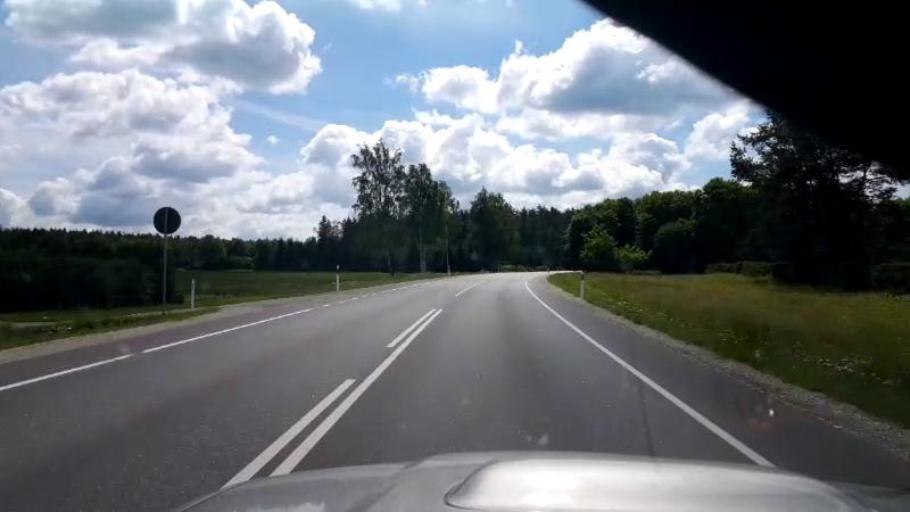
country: EE
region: Jaervamaa
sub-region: Jaerva-Jaani vald
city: Jarva-Jaani
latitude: 59.0510
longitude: 25.7048
